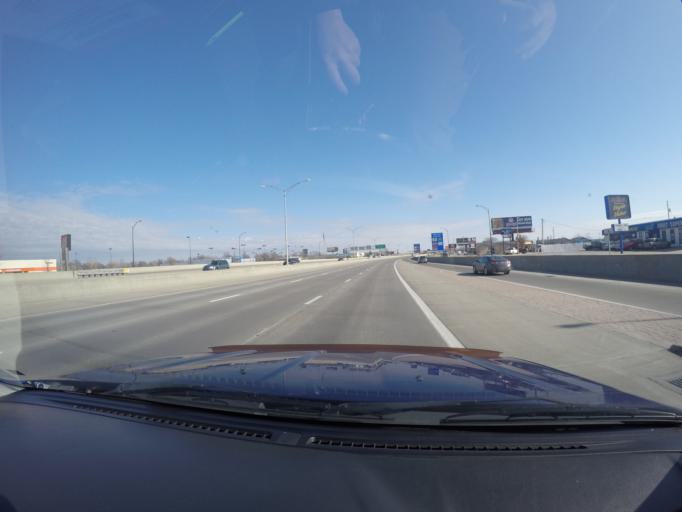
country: US
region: Kansas
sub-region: Sedgwick County
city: Wichita
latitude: 37.6717
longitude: -97.4398
